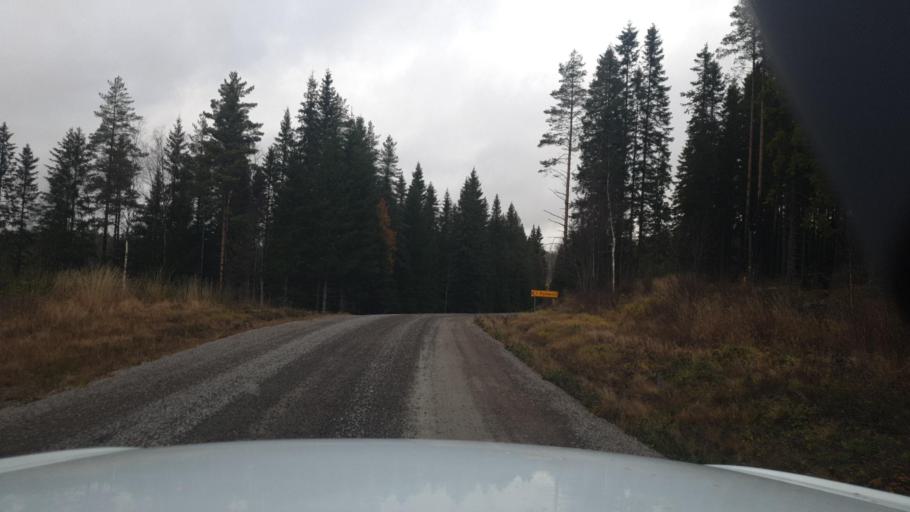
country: SE
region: Vaermland
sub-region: Eda Kommun
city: Charlottenberg
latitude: 60.0591
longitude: 12.6251
